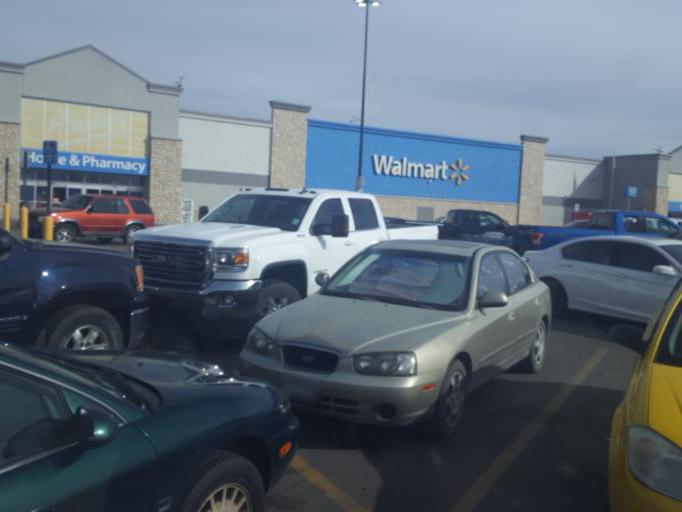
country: US
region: Colorado
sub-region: Alamosa County
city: Alamosa
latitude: 37.4813
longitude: -105.9045
